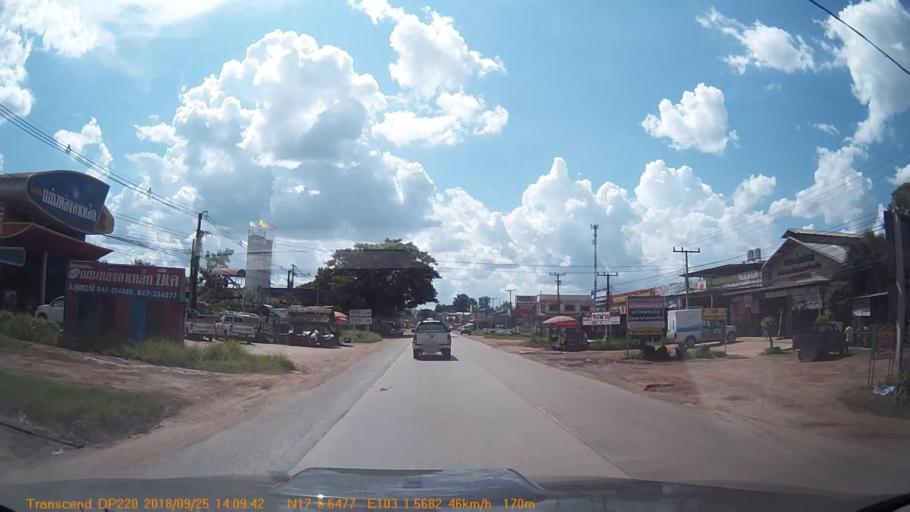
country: TH
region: Changwat Udon Thani
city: Kumphawapi
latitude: 17.1108
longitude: 103.0260
